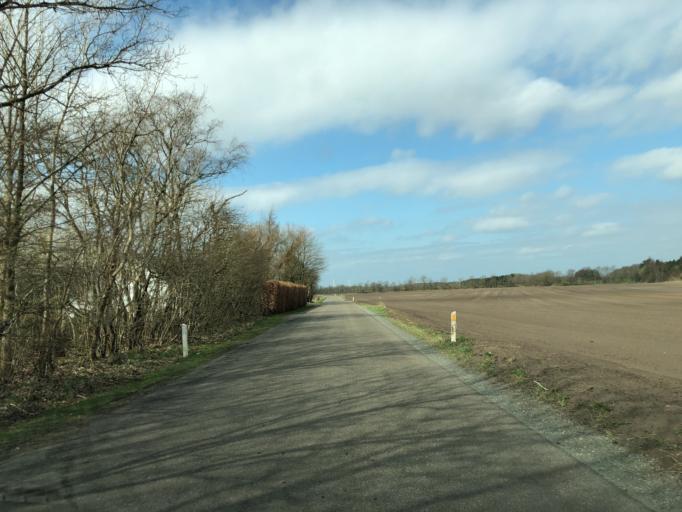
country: DK
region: South Denmark
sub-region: Vejle Kommune
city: Give
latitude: 55.9129
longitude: 9.2461
